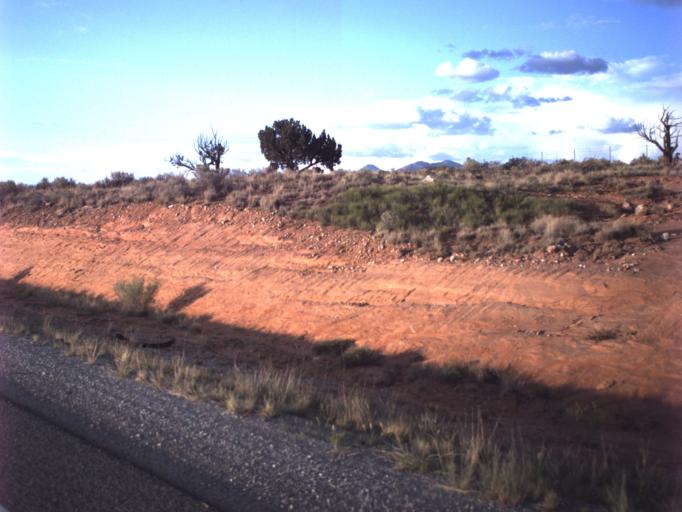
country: US
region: Utah
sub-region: Grand County
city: Moab
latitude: 38.2420
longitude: -109.3808
